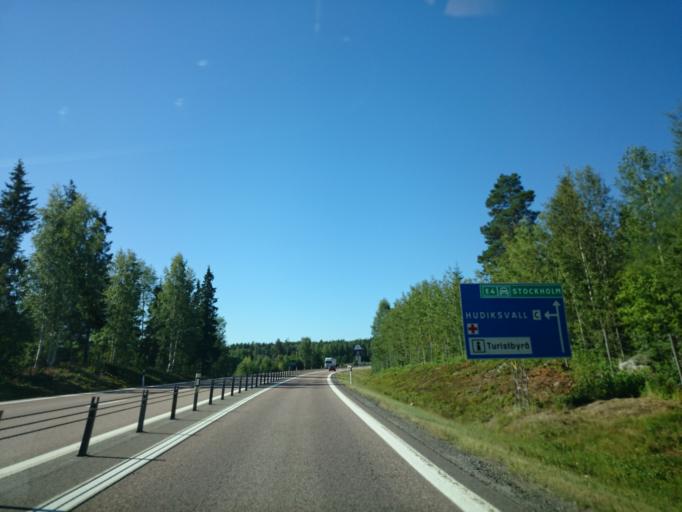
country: SE
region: Gaevleborg
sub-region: Hudiksvalls Kommun
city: Hudiksvall
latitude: 61.7463
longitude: 17.0782
